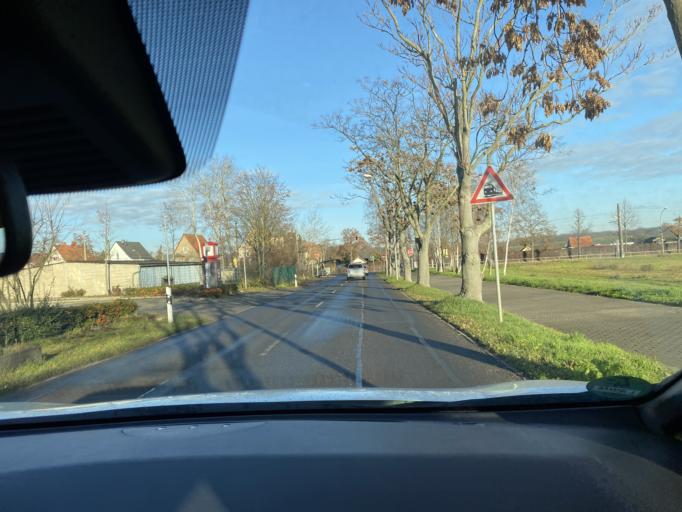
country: DE
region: Saxony
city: Schkeuditz
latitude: 51.3599
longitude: 12.2821
